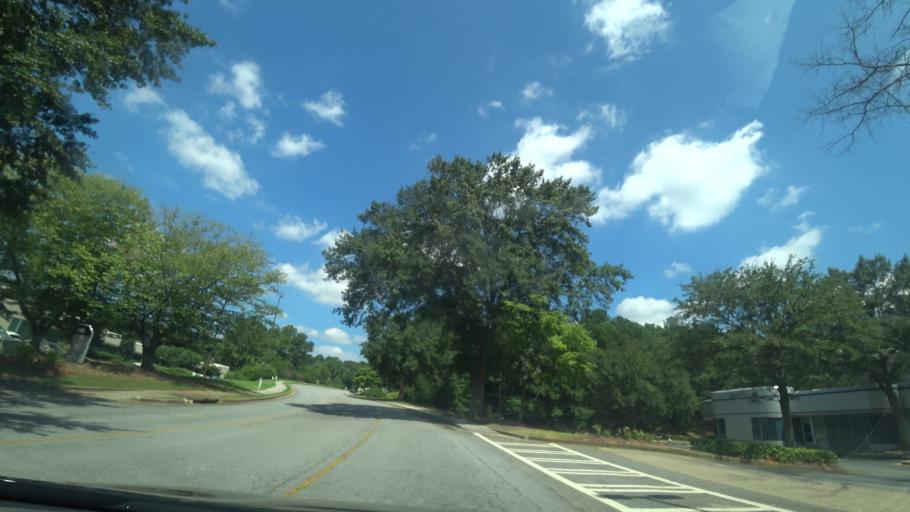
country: US
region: Georgia
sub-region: Gwinnett County
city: Norcross
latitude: 33.9300
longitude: -84.1844
